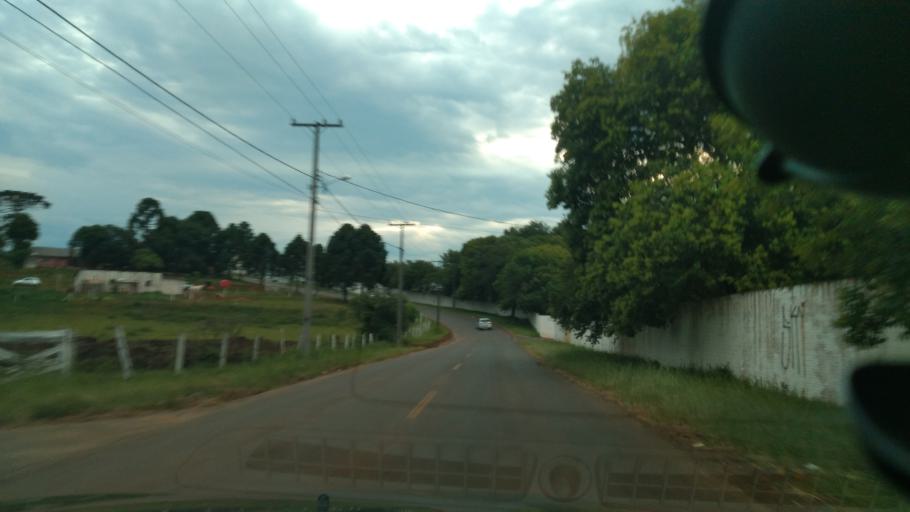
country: BR
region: Parana
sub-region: Guarapuava
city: Guarapuava
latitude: -25.3898
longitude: -51.4847
